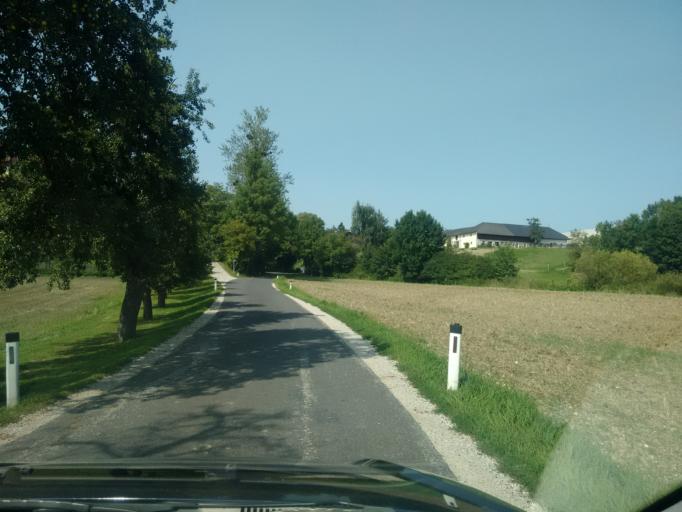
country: AT
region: Upper Austria
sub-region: Wels-Land
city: Gunskirchen
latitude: 48.1691
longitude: 13.9665
